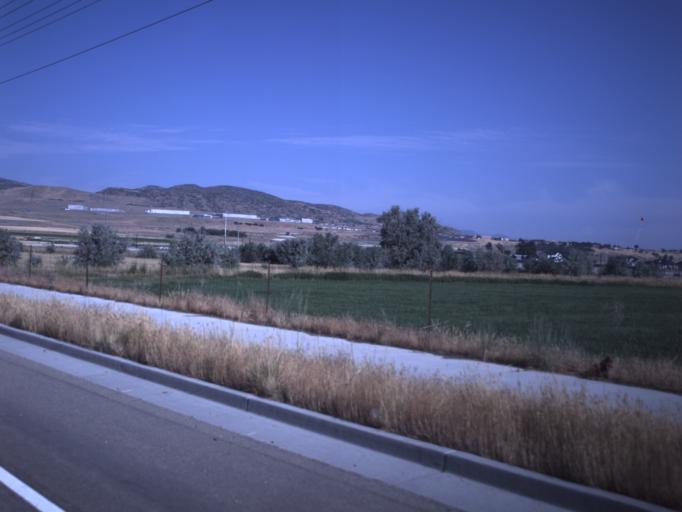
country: US
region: Utah
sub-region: Utah County
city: Lehi
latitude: 40.4132
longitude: -111.9011
